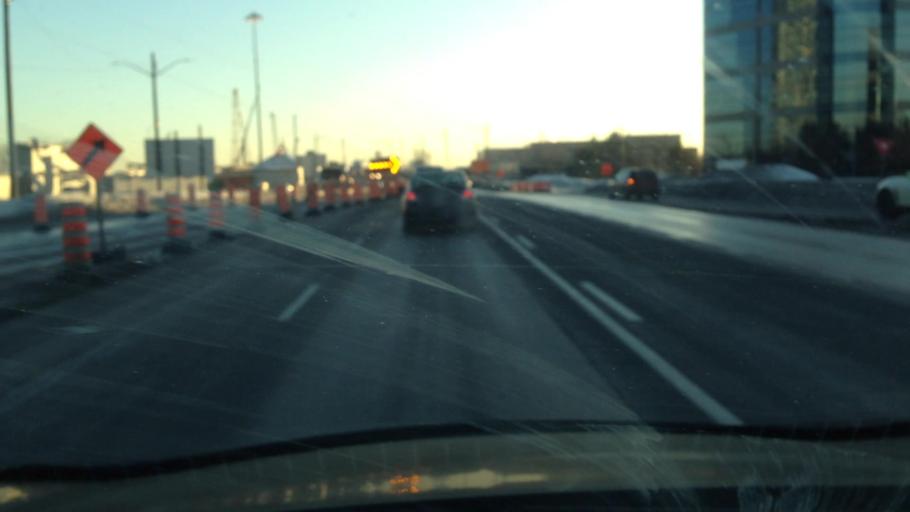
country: CA
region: Quebec
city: Westmount
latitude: 45.4701
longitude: -73.5409
